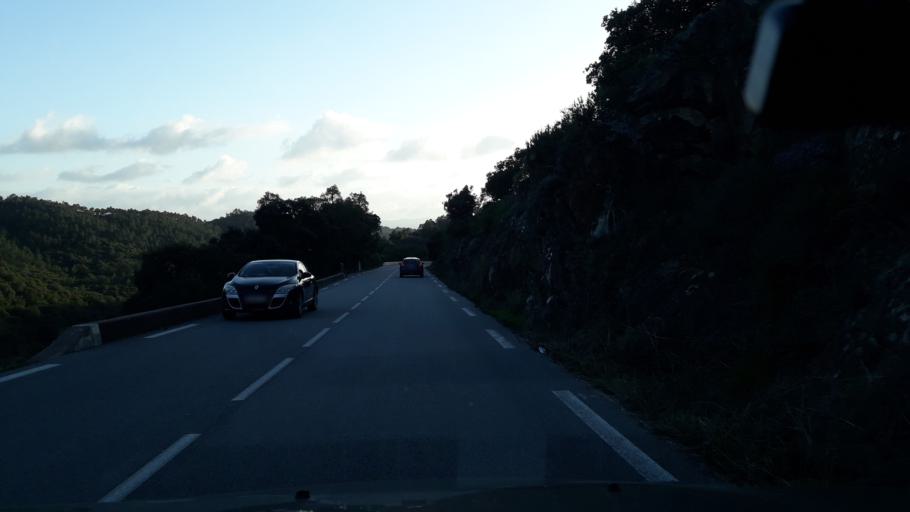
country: FR
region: Provence-Alpes-Cote d'Azur
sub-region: Departement du Var
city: Saint-Raphael
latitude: 43.4834
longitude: 6.7782
